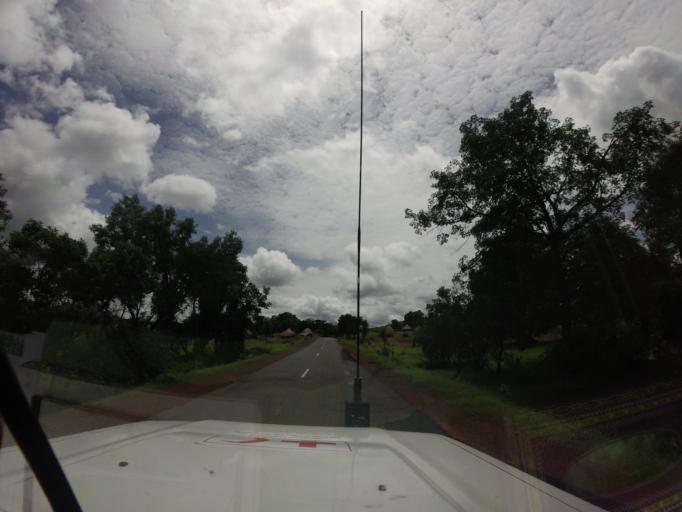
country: SL
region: Northern Province
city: Gberia Fotombu
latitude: 10.1015
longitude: -11.1478
